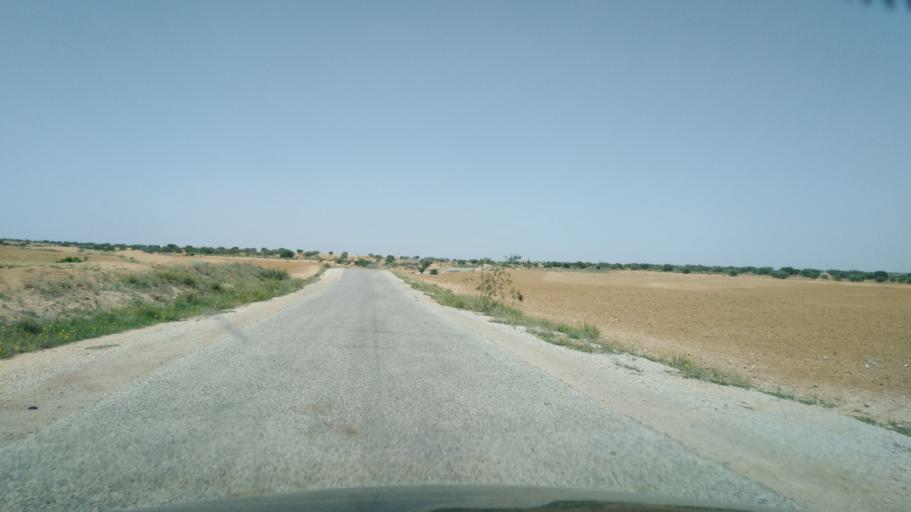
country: TN
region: Safaqis
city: Bi'r `Ali Bin Khalifah
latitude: 34.6786
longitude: 10.4147
